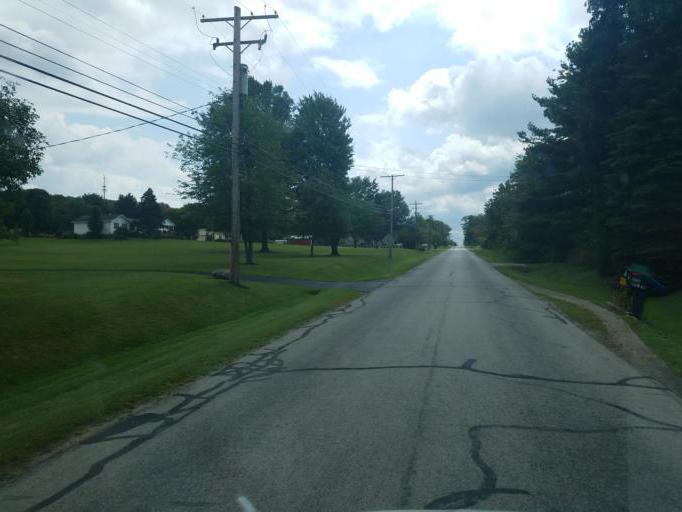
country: US
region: Ohio
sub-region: Geauga County
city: Middlefield
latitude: 41.5334
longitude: -81.0900
